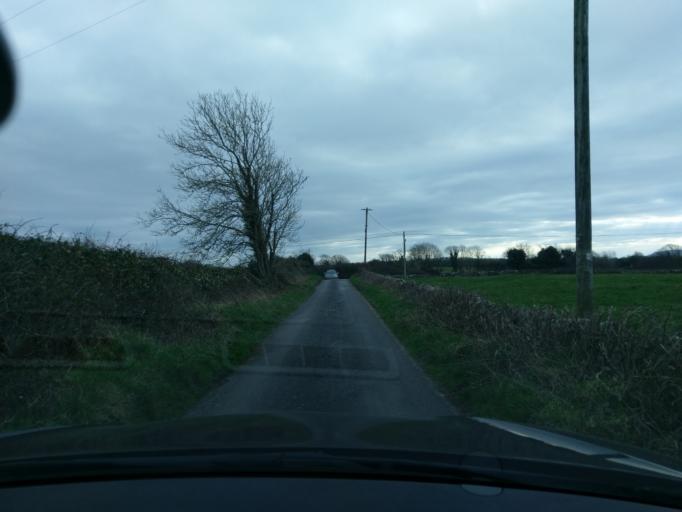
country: IE
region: Connaught
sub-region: County Galway
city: Oranmore
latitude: 53.2009
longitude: -8.9142
